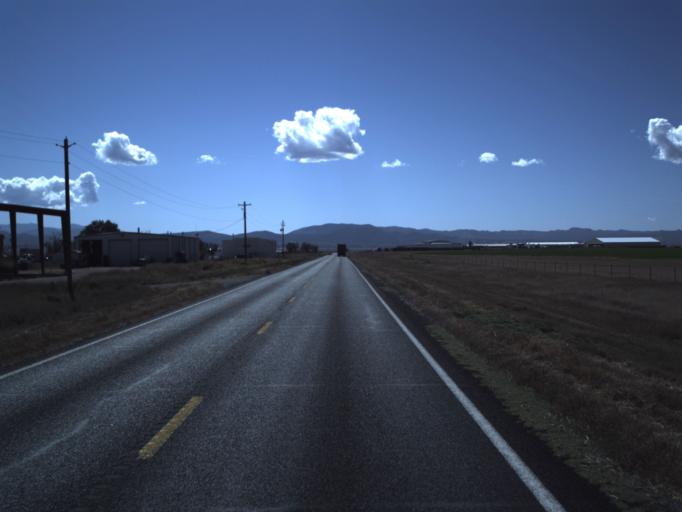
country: US
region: Utah
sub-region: Washington County
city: Enterprise
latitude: 37.6873
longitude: -113.6565
